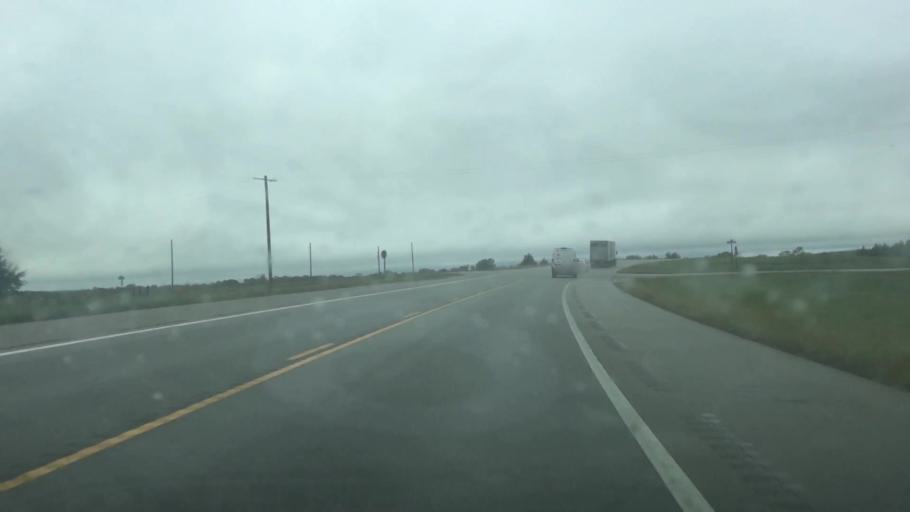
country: US
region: Kansas
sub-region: Anderson County
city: Garnett
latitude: 38.1644
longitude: -95.2975
